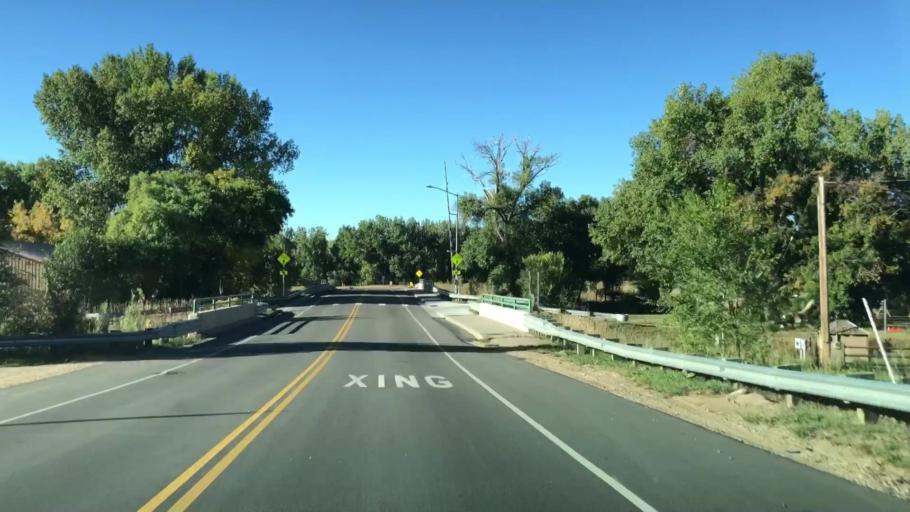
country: US
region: Colorado
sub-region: Larimer County
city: Loveland
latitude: 40.4057
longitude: -105.1408
